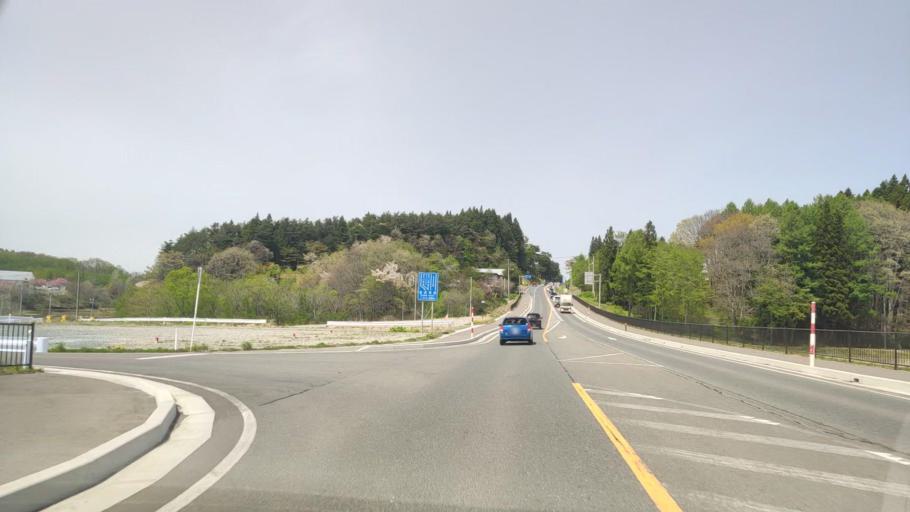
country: JP
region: Aomori
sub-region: Misawa Shi
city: Inuotose
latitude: 40.6641
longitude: 141.1873
